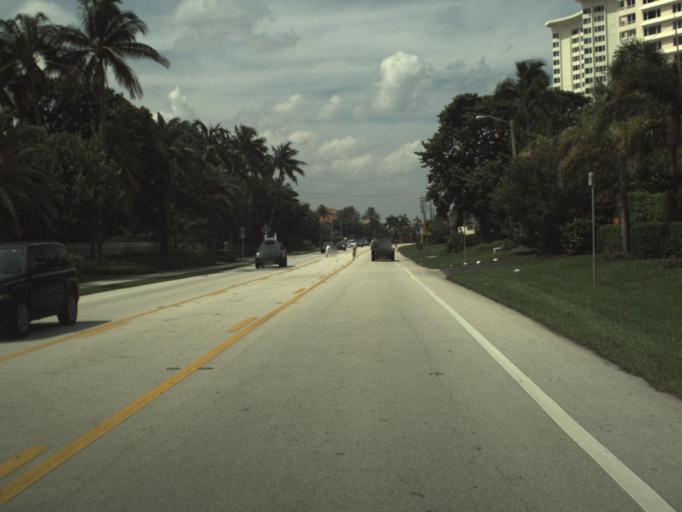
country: US
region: Florida
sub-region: Palm Beach County
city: Boca Raton
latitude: 26.3420
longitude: -80.0718
